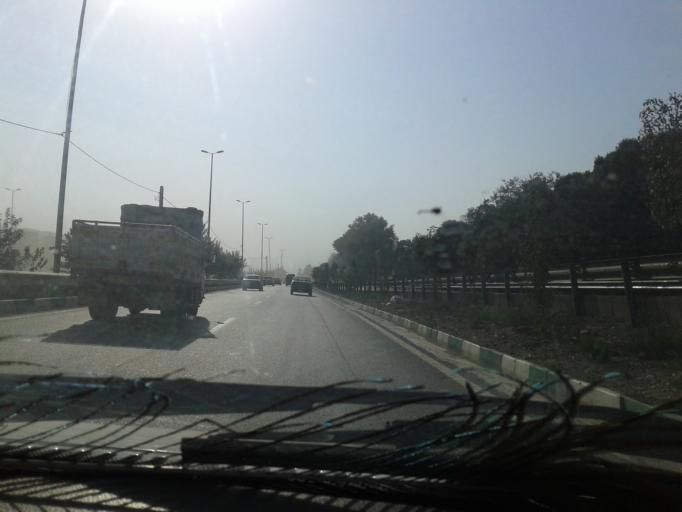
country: IR
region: Tehran
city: Tehran
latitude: 35.7240
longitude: 51.5985
